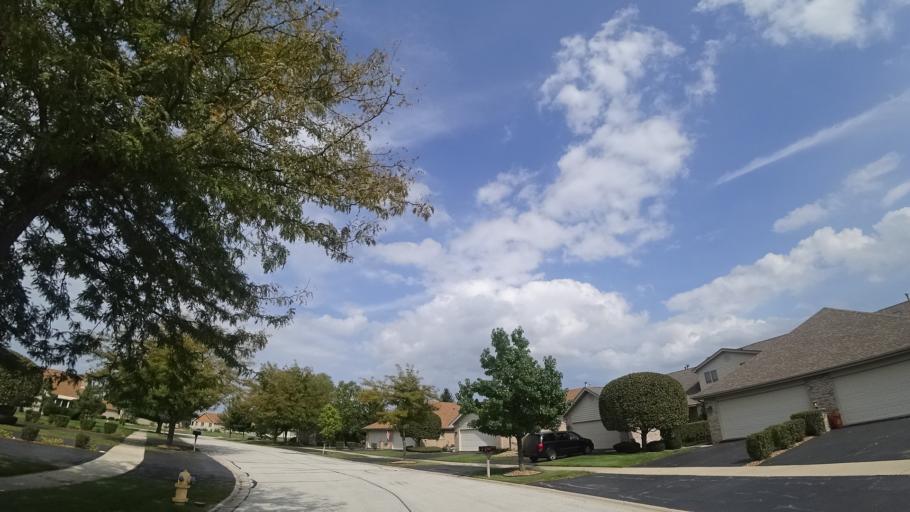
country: US
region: Illinois
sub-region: Cook County
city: Tinley Park
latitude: 41.5553
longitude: -87.7766
